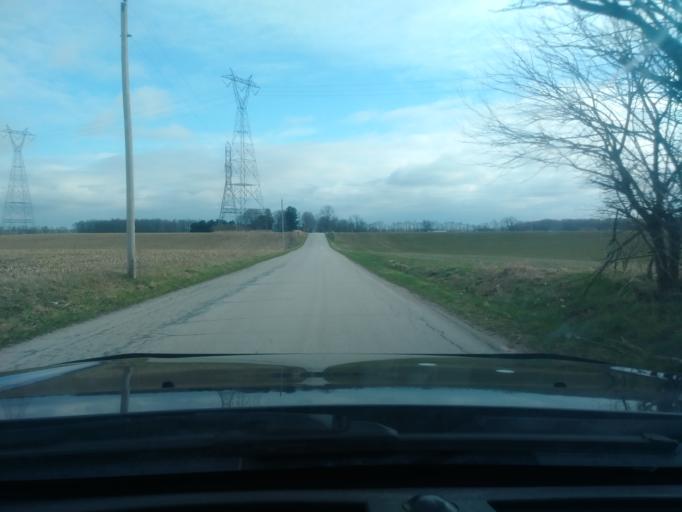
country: US
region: Indiana
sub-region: LaPorte County
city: LaPorte
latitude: 41.5507
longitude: -86.7986
